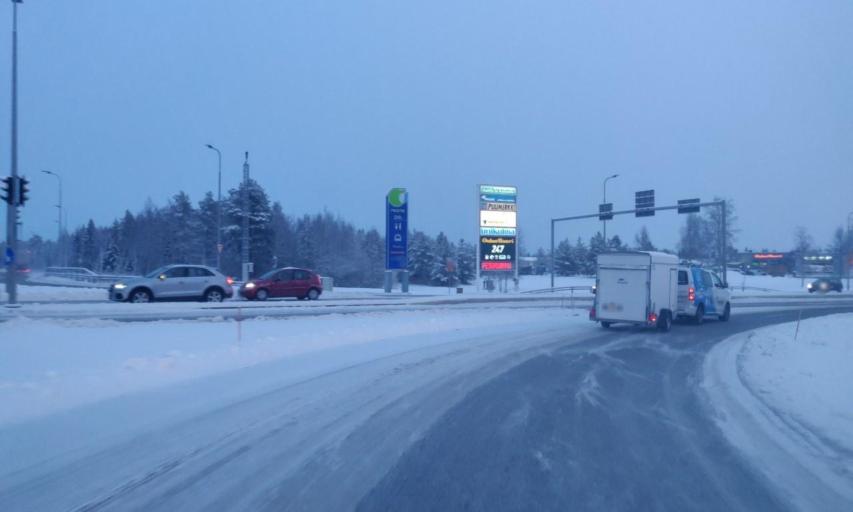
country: FI
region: Northern Ostrobothnia
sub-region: Oulu
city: Kempele
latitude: 64.9807
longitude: 25.5606
